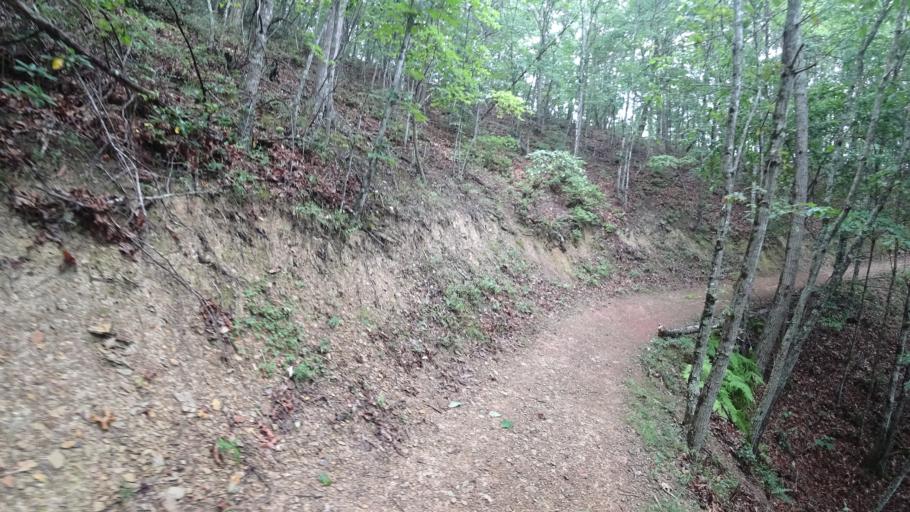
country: US
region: Virginia
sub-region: Smyth County
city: Marion
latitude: 36.8826
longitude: -81.5218
